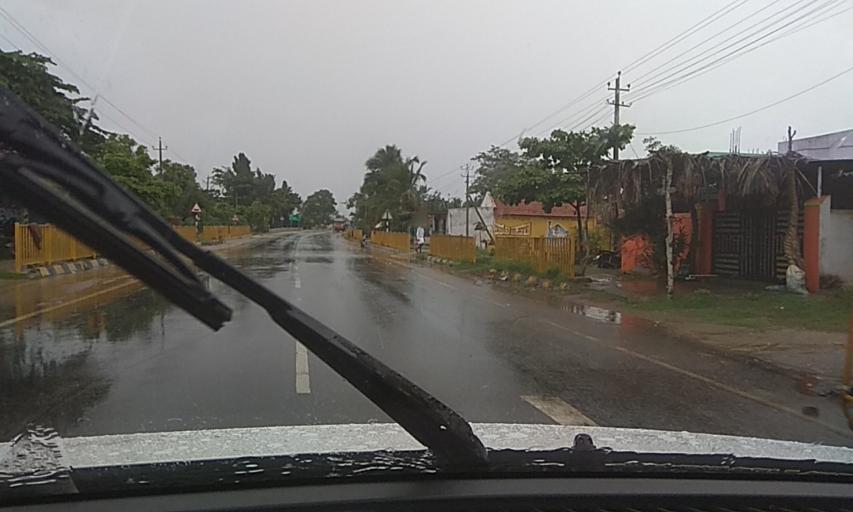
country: IN
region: Karnataka
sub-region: Mandya
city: Maddur
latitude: 12.7376
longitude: 77.0600
